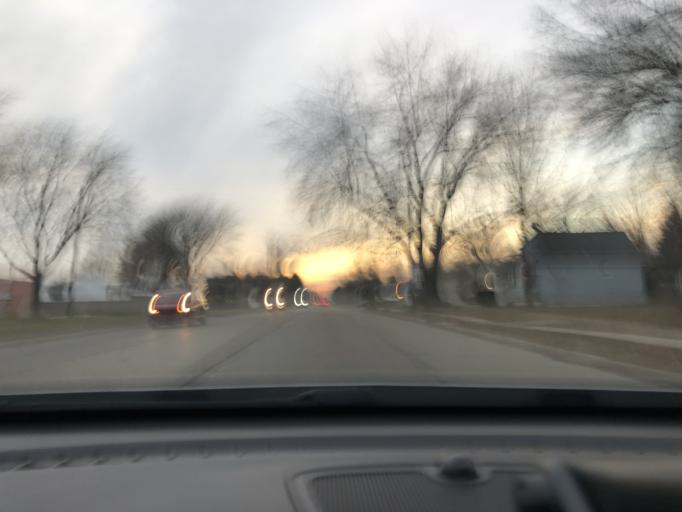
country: US
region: Michigan
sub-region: Wayne County
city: Taylor
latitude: 42.2415
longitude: -83.2561
